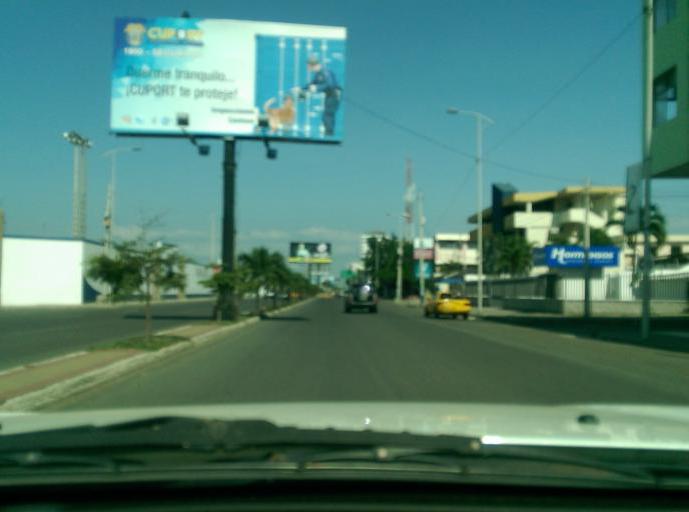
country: EC
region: Manabi
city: Manta
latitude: -0.9420
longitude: -80.7267
